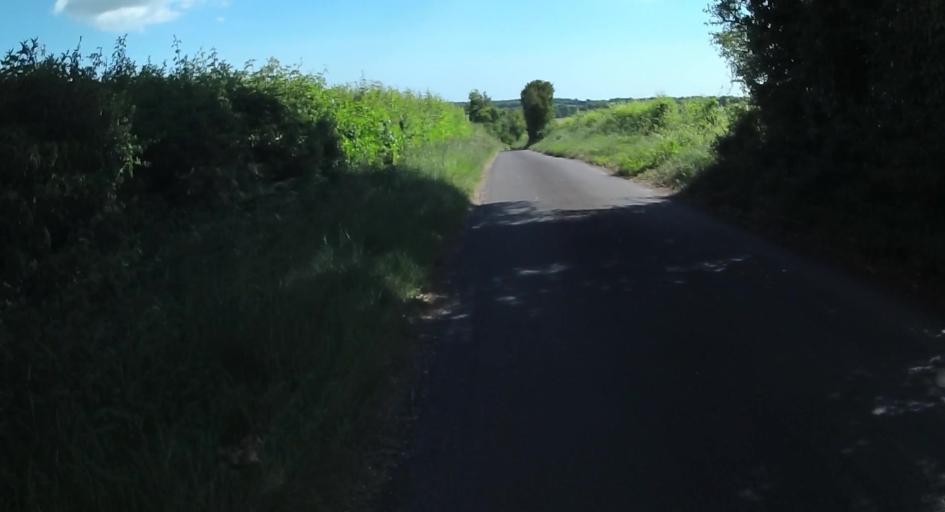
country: GB
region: England
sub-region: Hampshire
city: Old Basing
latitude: 51.2227
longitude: -1.0245
